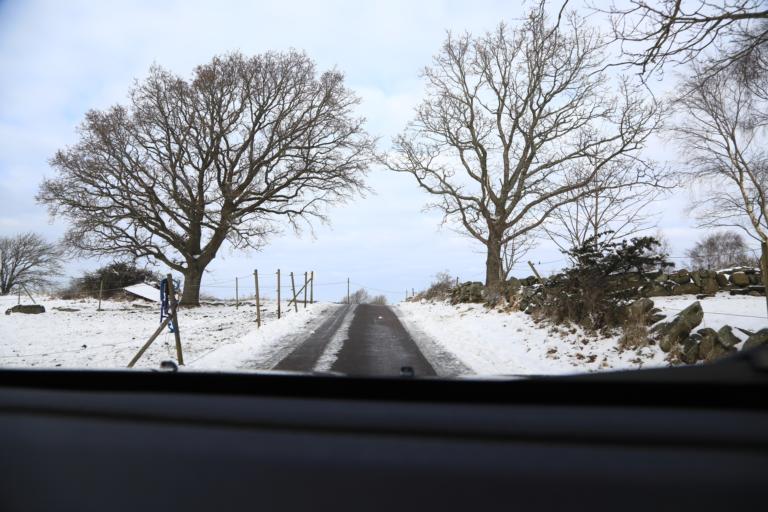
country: SE
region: Halland
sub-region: Kungsbacka Kommun
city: Frillesas
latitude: 57.2318
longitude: 12.1911
